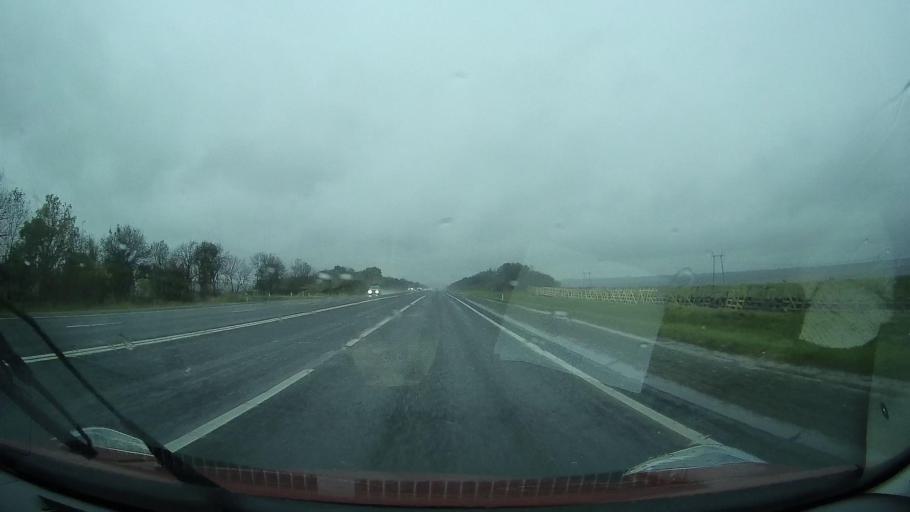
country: RU
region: Stavropol'skiy
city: Nevinnomyssk
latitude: 44.6150
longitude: 42.1090
